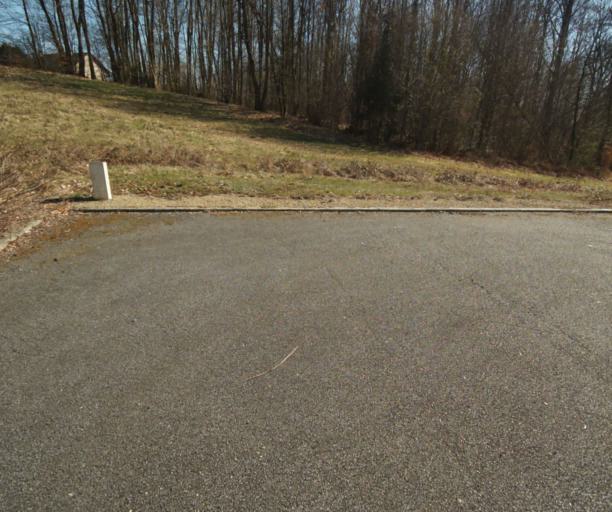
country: FR
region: Limousin
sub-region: Departement de la Correze
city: Chamboulive
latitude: 45.4689
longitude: 1.7443
